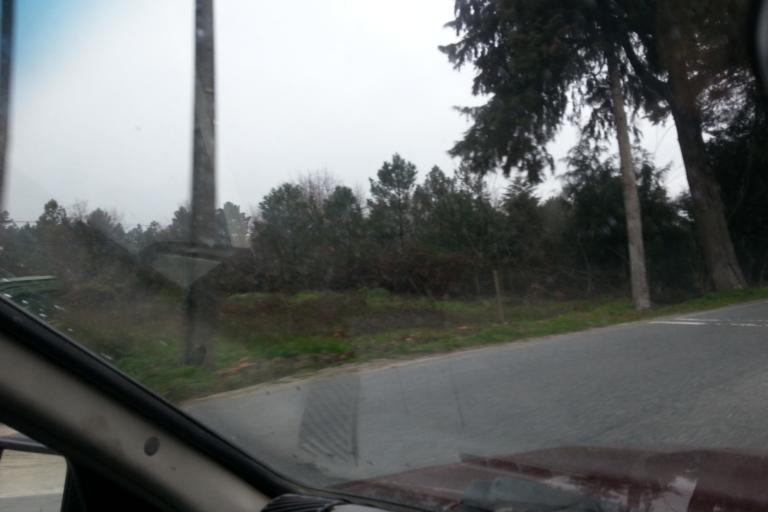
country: PT
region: Viseu
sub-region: Mangualde
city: Mangualde
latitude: 40.6080
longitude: -7.7343
